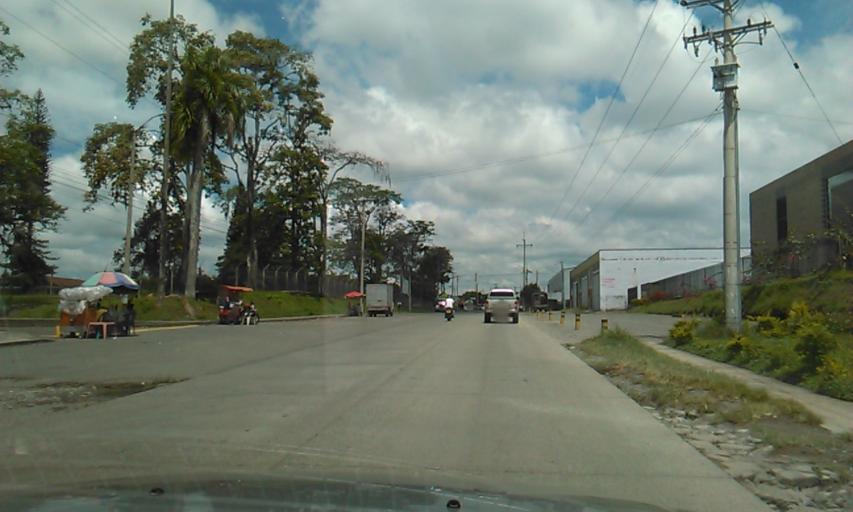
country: CO
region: Quindio
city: Armenia
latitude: 4.5065
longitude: -75.6910
